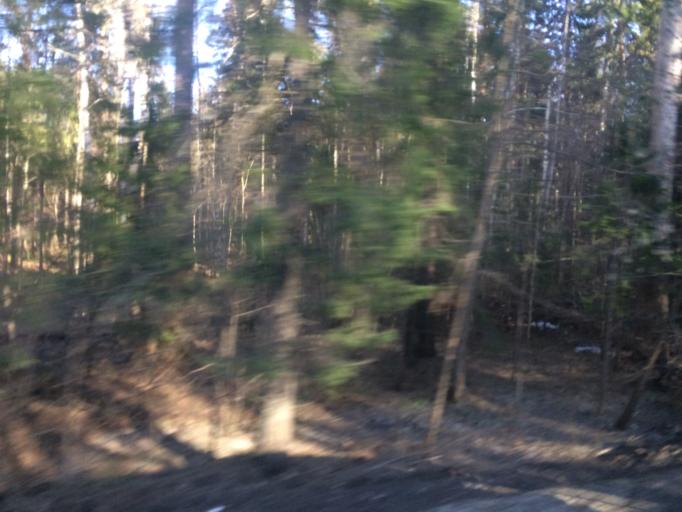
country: RU
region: Tatarstan
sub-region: Zelenodol'skiy Rayon
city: Vasil'yevo
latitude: 55.8959
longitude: 48.7292
